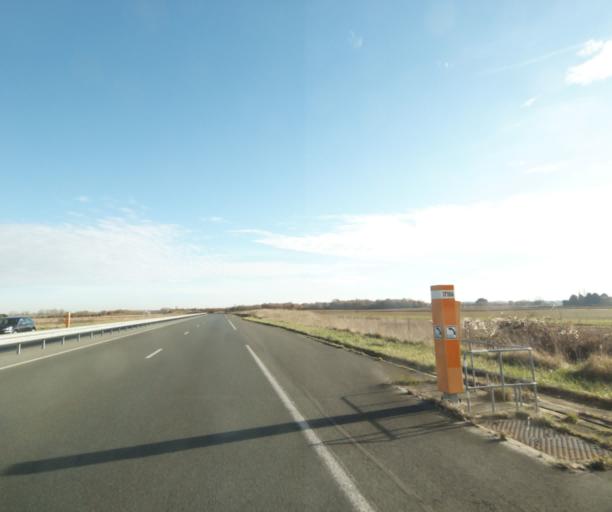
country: FR
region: Poitou-Charentes
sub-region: Departement de la Charente-Maritime
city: Saint-Romain-de-Benet
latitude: 45.6975
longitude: -0.8067
